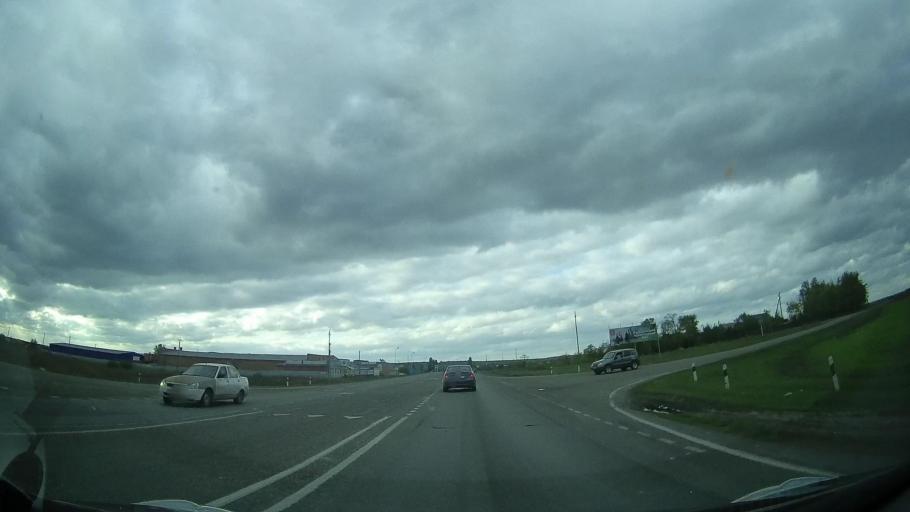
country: RU
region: Rostov
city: Kagal'nitskaya
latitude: 46.8744
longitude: 40.1617
